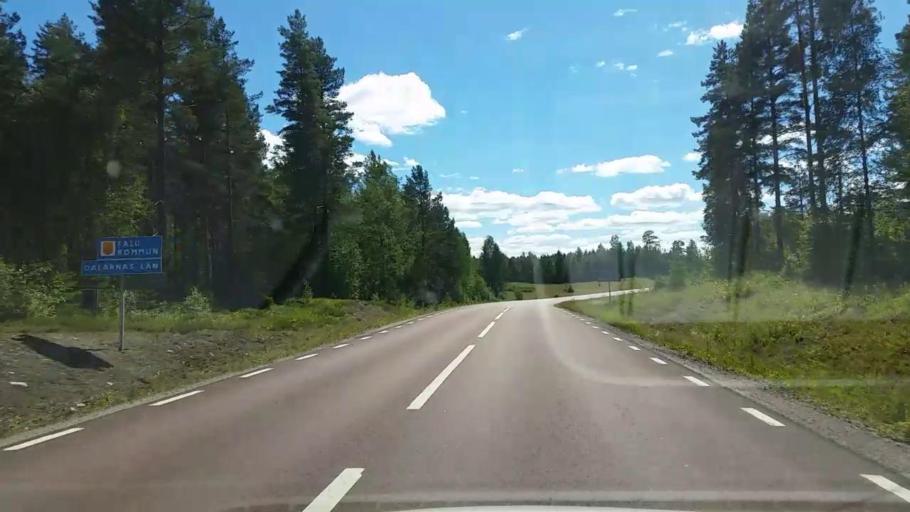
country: SE
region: Gaevleborg
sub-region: Bollnas Kommun
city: Vittsjo
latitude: 61.0421
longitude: 15.7918
